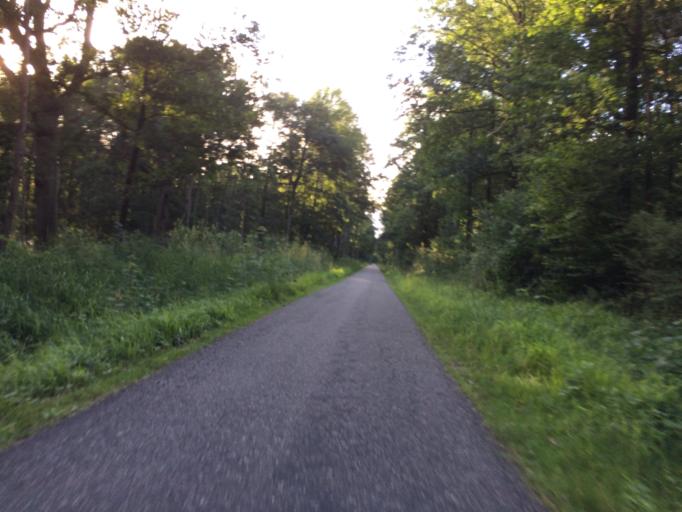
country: FR
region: Ile-de-France
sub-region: Departement de l'Essonne
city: Soisy-sur-Seine
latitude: 48.6648
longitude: 2.4705
